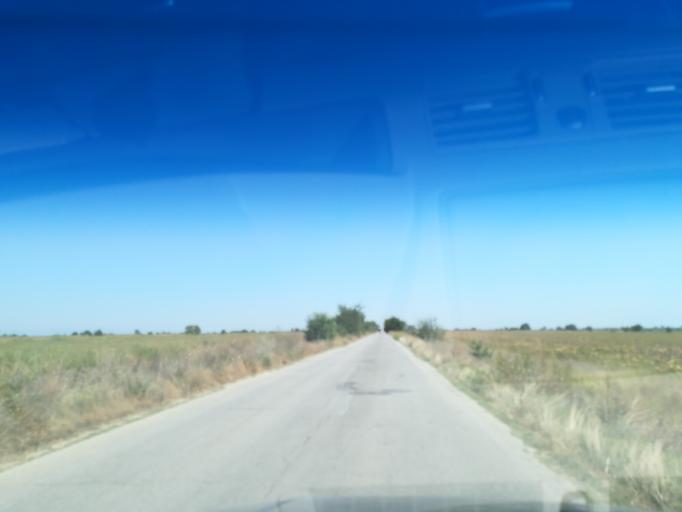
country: BG
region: Plovdiv
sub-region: Obshtina Suedinenie
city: Suedinenie
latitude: 42.2515
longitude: 24.4646
